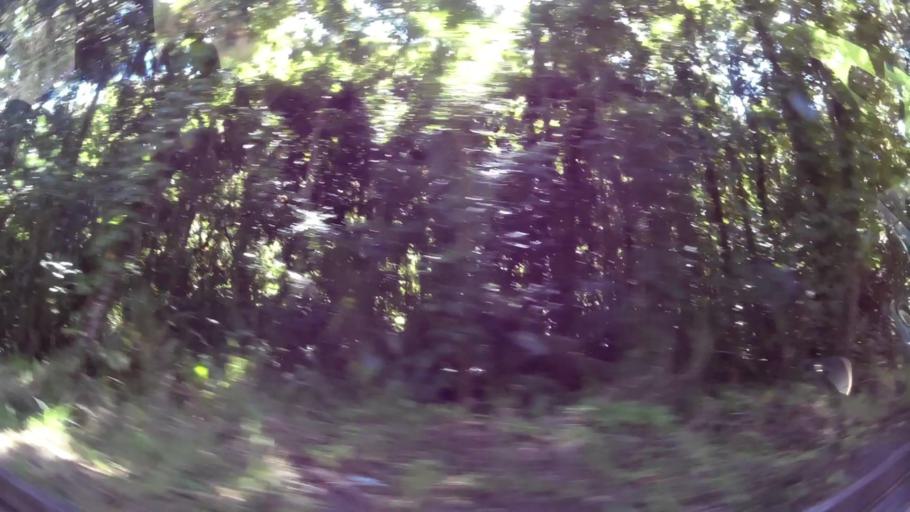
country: DM
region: Saint Paul
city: Mahaut
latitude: 15.3428
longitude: -61.3736
